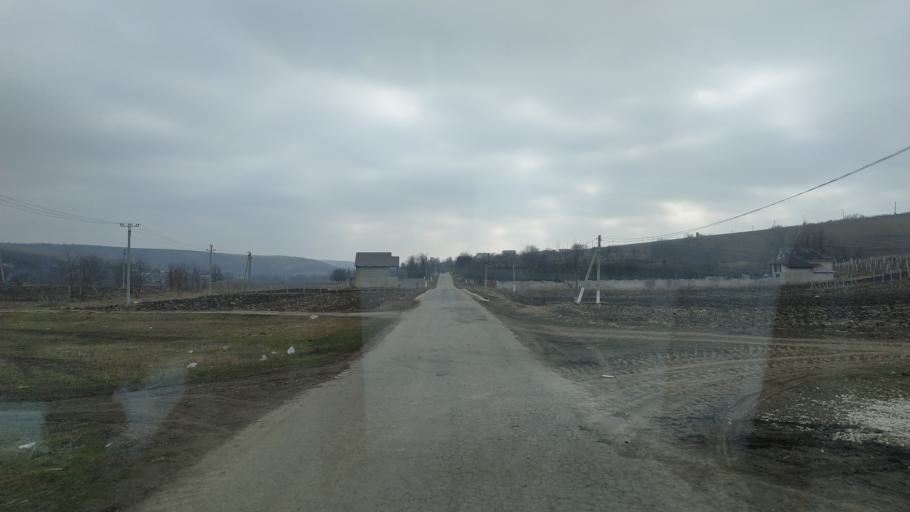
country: MD
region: Hincesti
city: Dancu
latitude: 46.8942
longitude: 28.3247
